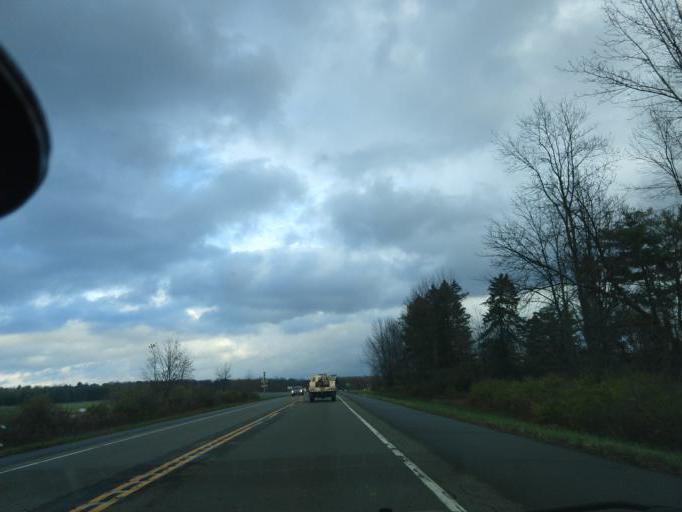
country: US
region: New York
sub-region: Tompkins County
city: Northeast Ithaca
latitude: 42.4829
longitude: -76.4529
